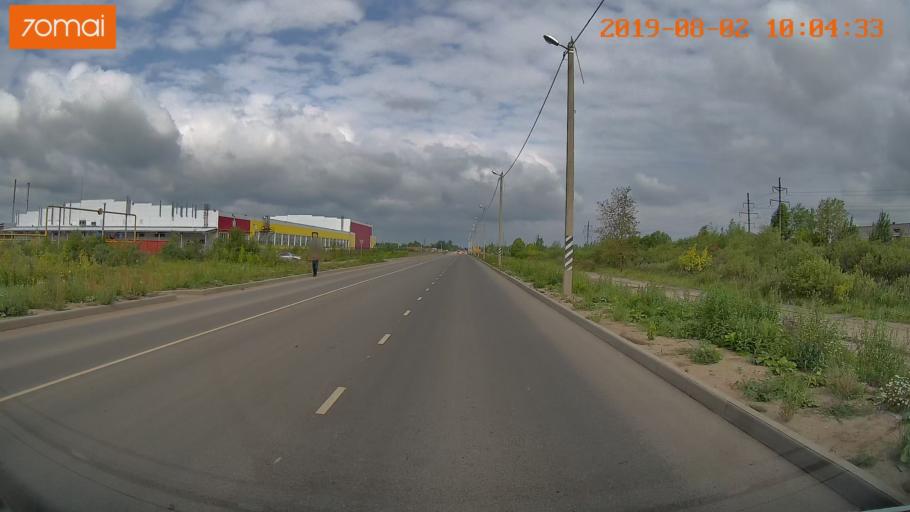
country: RU
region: Ivanovo
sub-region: Gorod Ivanovo
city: Ivanovo
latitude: 56.9733
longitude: 40.9249
